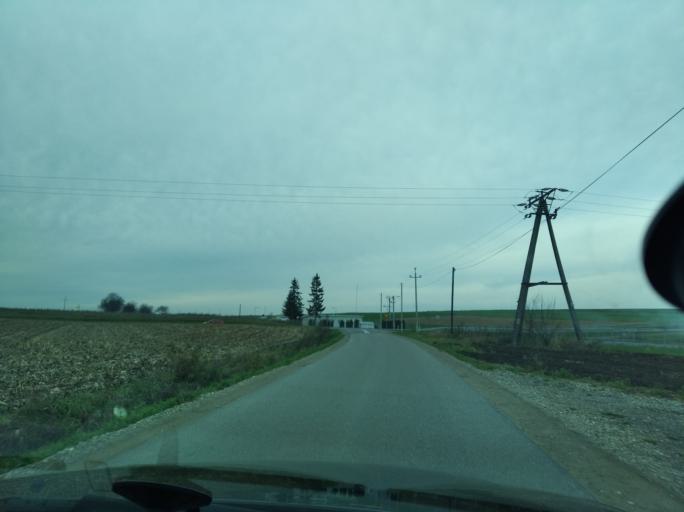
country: PL
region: Subcarpathian Voivodeship
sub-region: Powiat przeworski
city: Przeworsk
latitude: 50.0645
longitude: 22.4712
